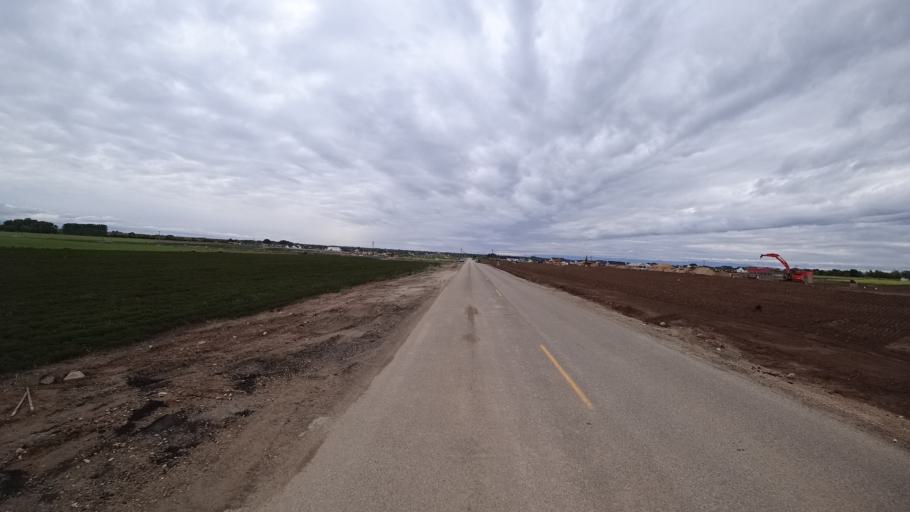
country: US
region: Idaho
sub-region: Ada County
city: Eagle
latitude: 43.7195
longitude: -116.4234
